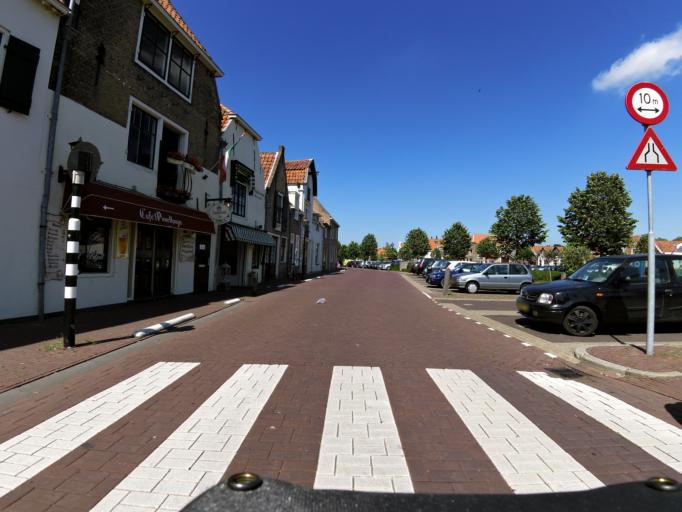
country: NL
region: South Holland
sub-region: Gemeente Brielle
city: Brielle
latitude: 51.9019
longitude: 4.1665
